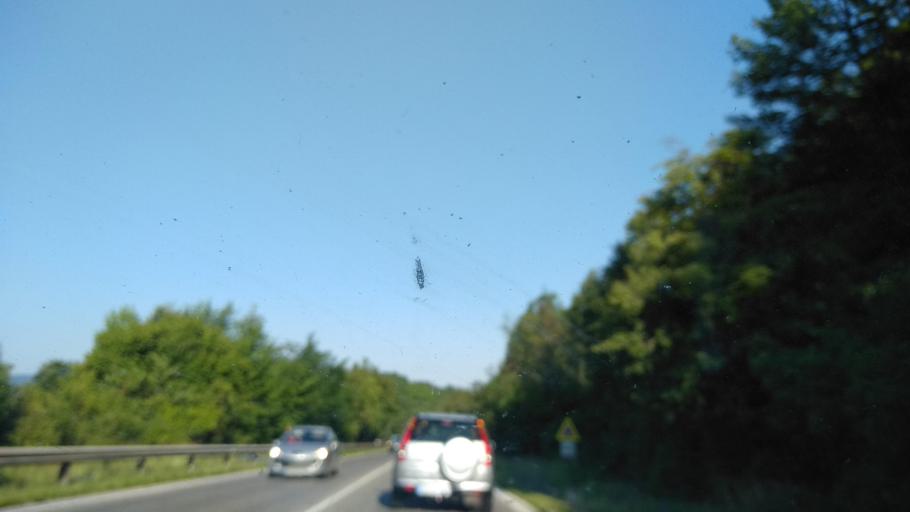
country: BG
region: Lovech
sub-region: Obshtina Lovech
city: Lovech
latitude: 43.0489
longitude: 24.7968
